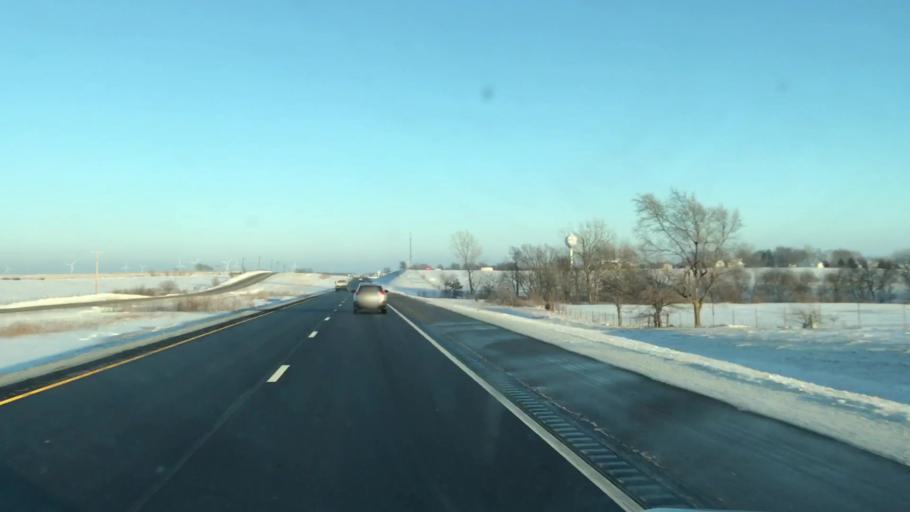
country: US
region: Missouri
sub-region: Clinton County
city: Gower
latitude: 39.7620
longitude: -94.5157
